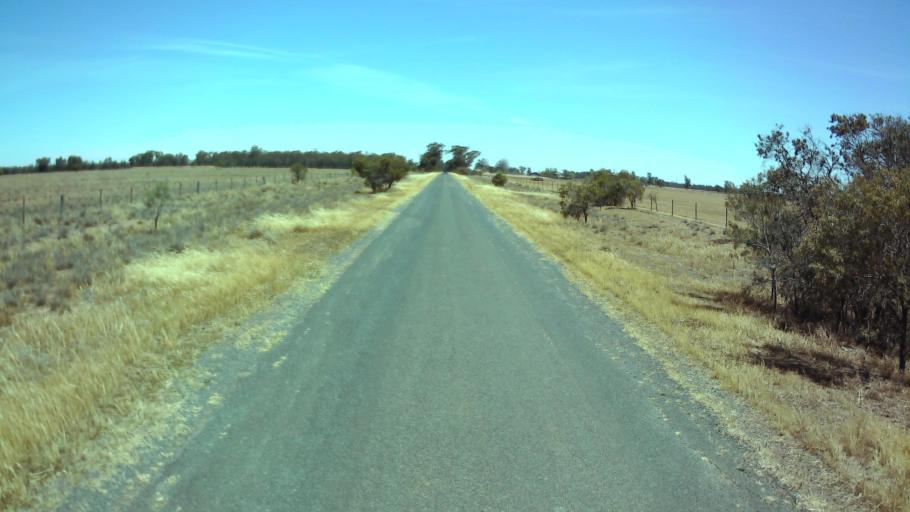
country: AU
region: New South Wales
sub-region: Weddin
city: Grenfell
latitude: -33.8962
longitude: 147.6872
